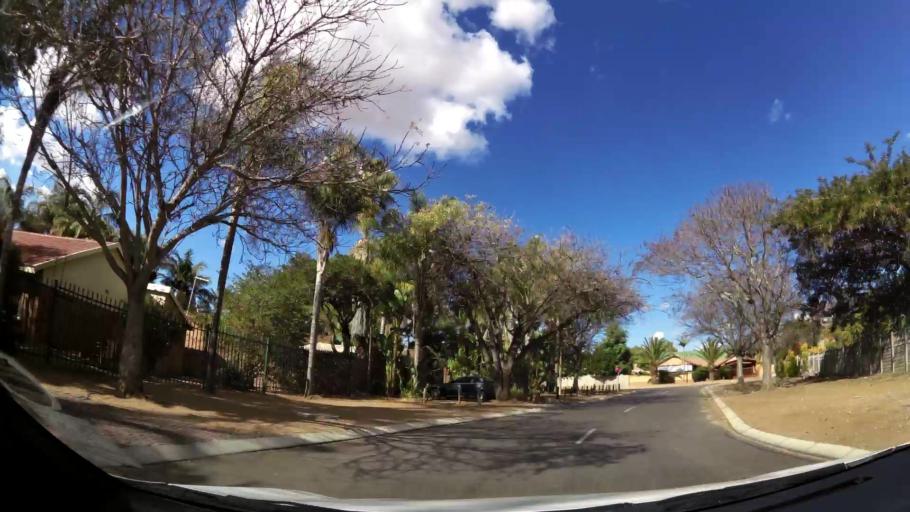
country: ZA
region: Limpopo
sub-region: Capricorn District Municipality
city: Polokwane
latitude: -23.8819
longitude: 29.4691
